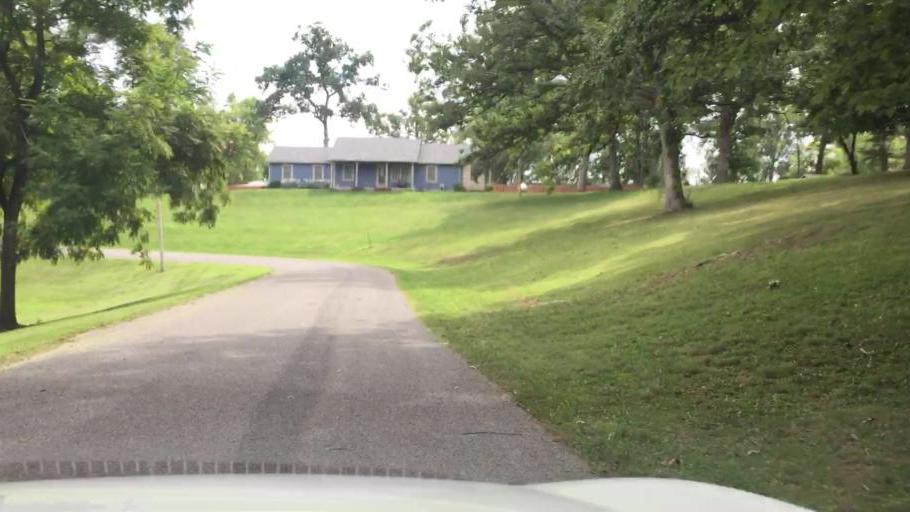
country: US
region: Ohio
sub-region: Champaign County
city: Urbana
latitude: 40.0973
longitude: -83.7048
